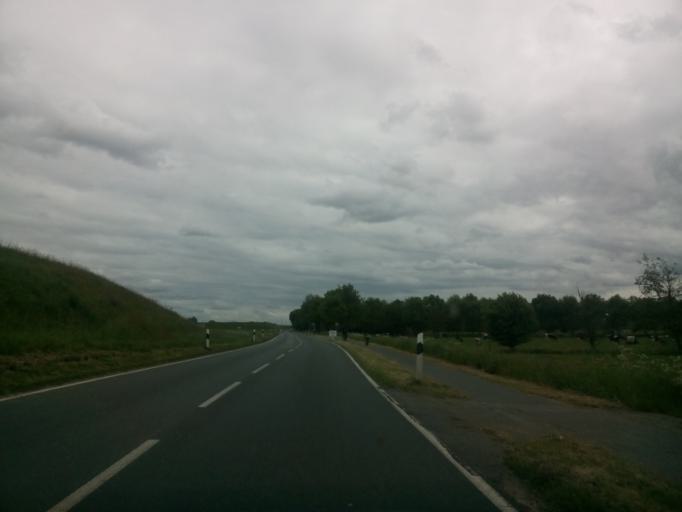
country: DE
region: Lower Saxony
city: Lemwerder
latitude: 53.1202
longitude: 8.6405
